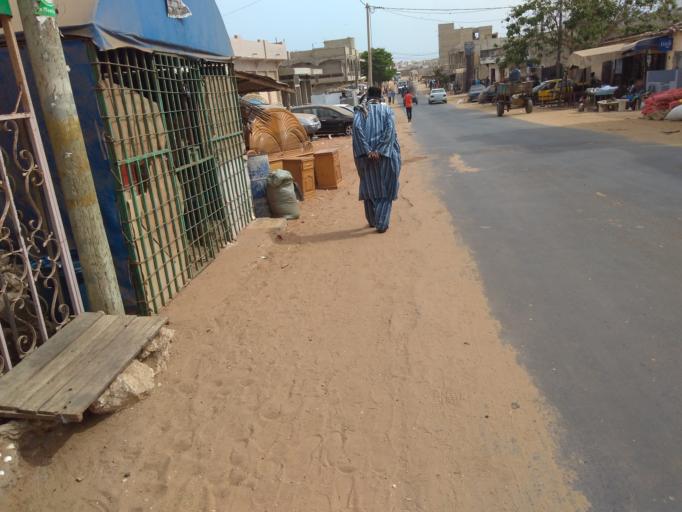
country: SN
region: Dakar
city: Pikine
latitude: 14.7970
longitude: -17.3369
